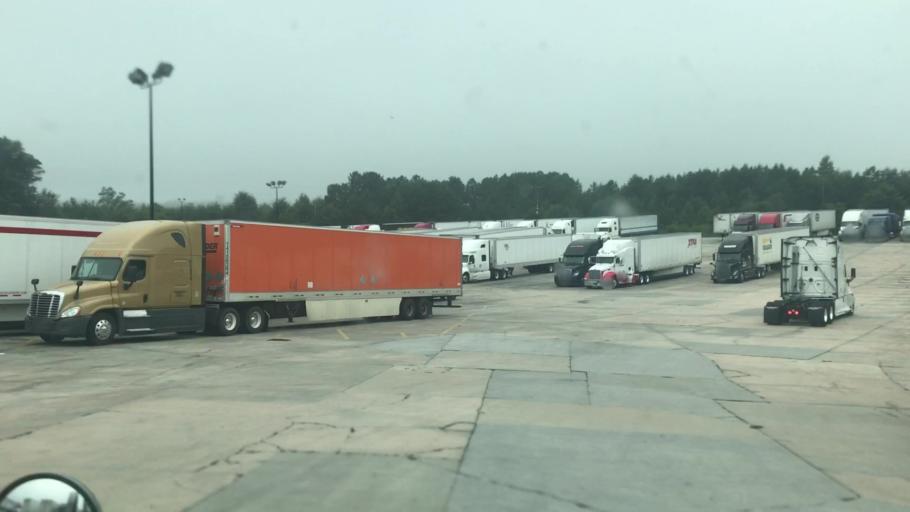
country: US
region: Georgia
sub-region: Butts County
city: Jackson
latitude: 33.2081
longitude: -84.0651
